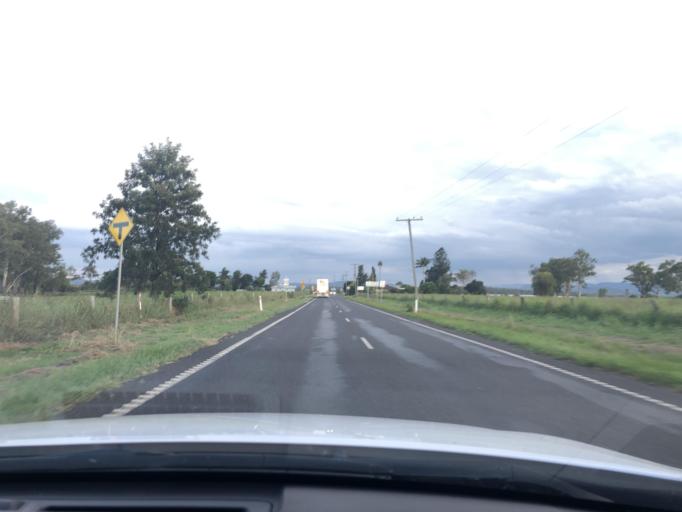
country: AU
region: Queensland
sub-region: Lockyer Valley
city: Gatton
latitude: -27.5812
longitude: 152.3627
